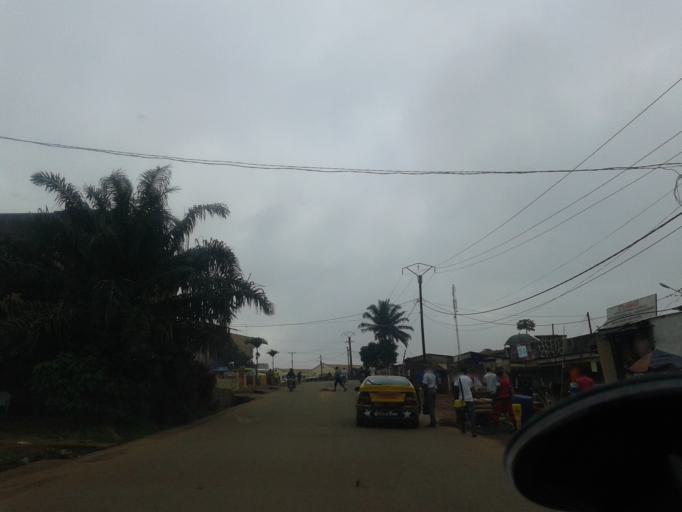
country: CM
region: Centre
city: Yaounde
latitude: 3.9099
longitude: 11.5276
